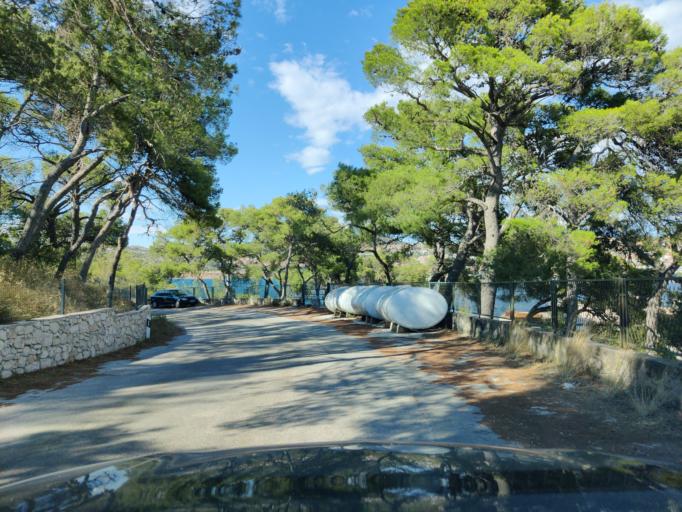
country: HR
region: Sibensko-Kniniska
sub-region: Grad Sibenik
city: Sibenik
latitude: 43.7361
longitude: 15.8761
